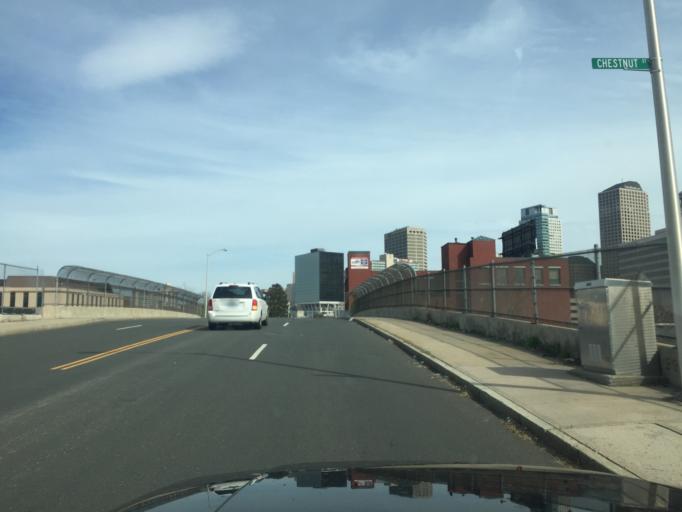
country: US
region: Connecticut
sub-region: Hartford County
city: Hartford
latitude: 41.7727
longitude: -72.6814
